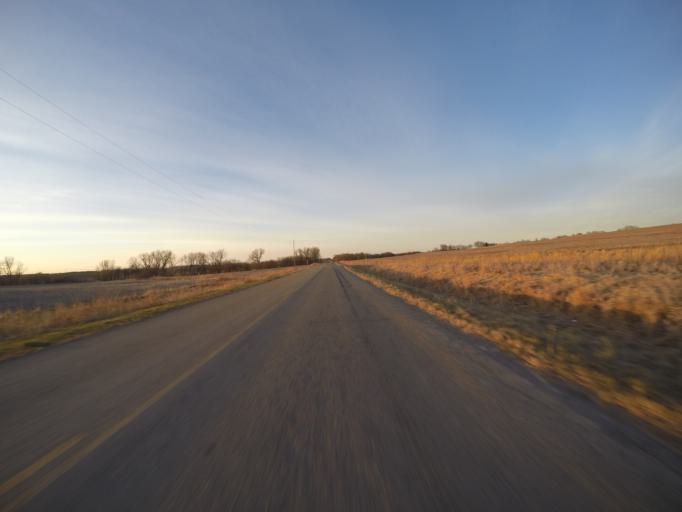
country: US
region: Kansas
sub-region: Clay County
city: Clay Center
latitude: 39.4491
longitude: -96.9981
